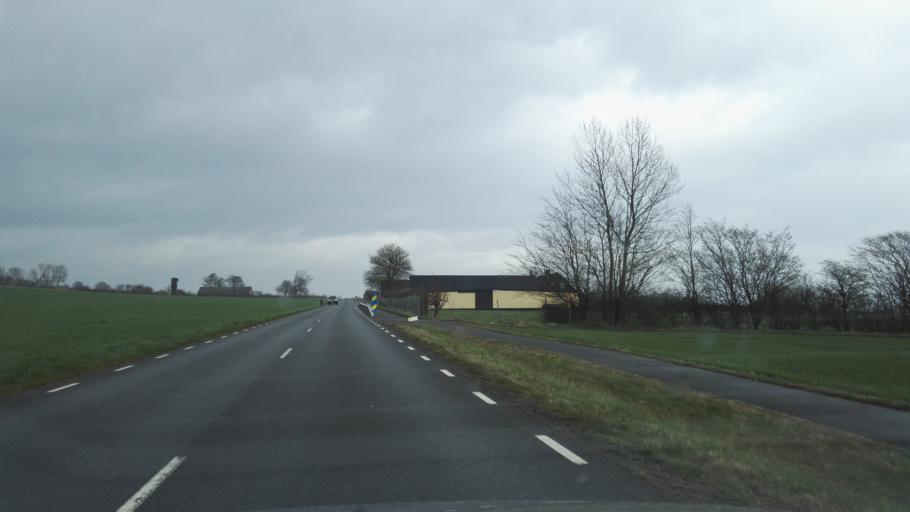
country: SE
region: Skane
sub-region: Simrishamns Kommun
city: Simrishamn
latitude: 55.4860
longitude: 14.2946
